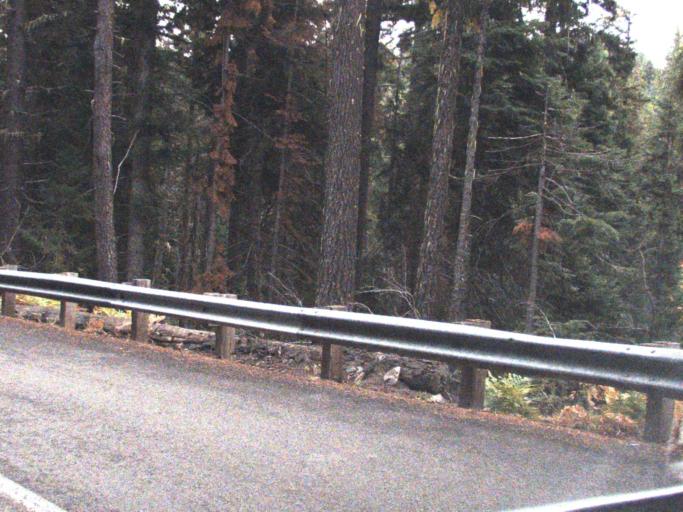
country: US
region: Washington
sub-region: Yakima County
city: Tieton
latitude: 46.6517
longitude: -121.2922
